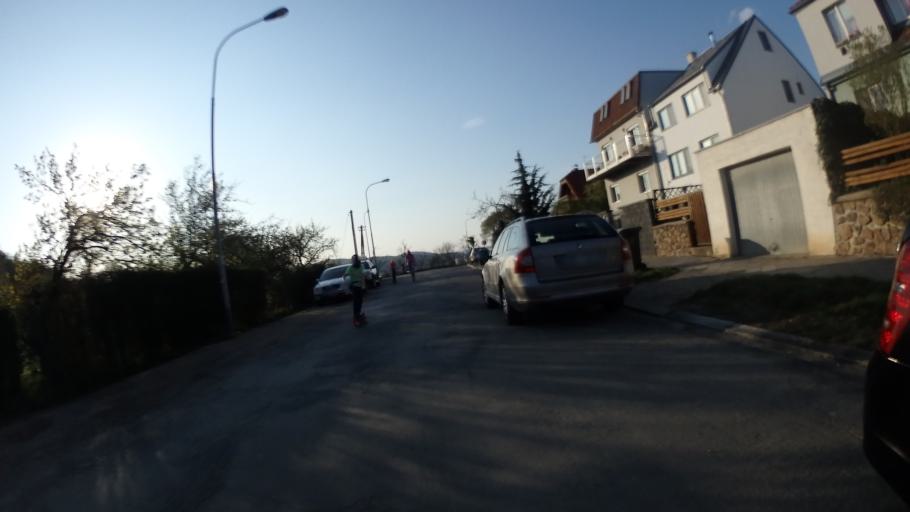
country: CZ
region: South Moravian
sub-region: Mesto Brno
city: Brno
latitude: 49.1824
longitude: 16.5878
